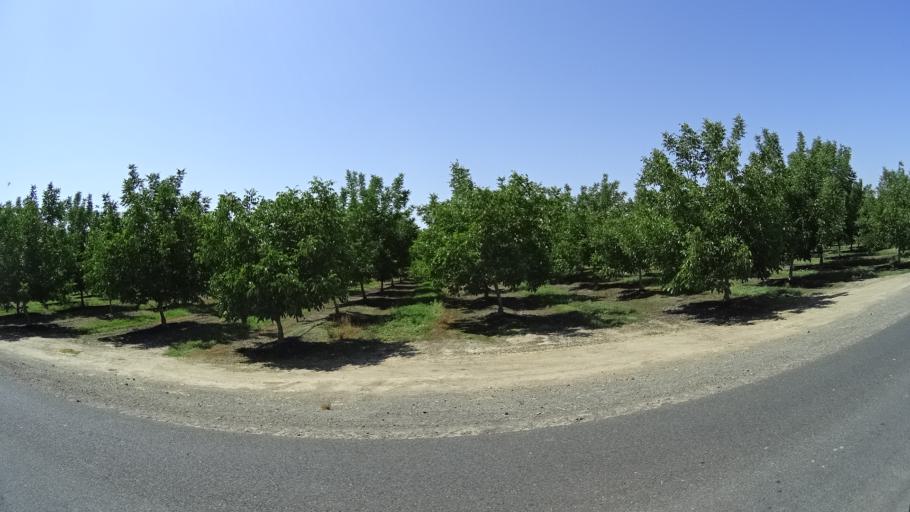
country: US
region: California
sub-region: Kings County
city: Lucerne
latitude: 36.3717
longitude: -119.7020
